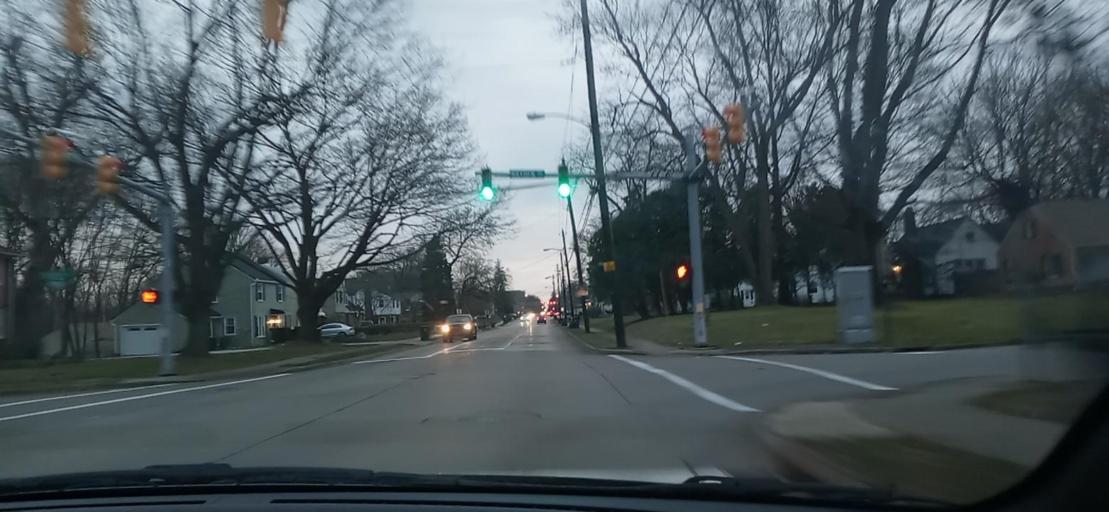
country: US
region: Ohio
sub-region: Summit County
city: Fairlawn
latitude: 41.1135
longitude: -81.5692
